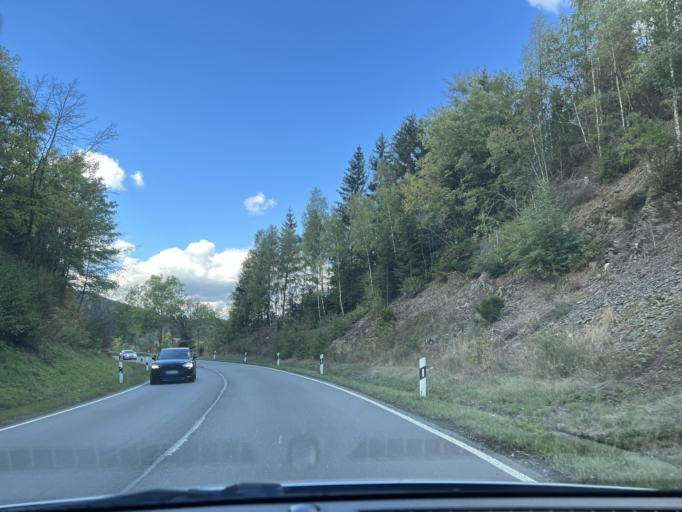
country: DE
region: North Rhine-Westphalia
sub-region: Regierungsbezirk Arnsberg
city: Bad Berleburg
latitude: 51.0212
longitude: 8.3984
